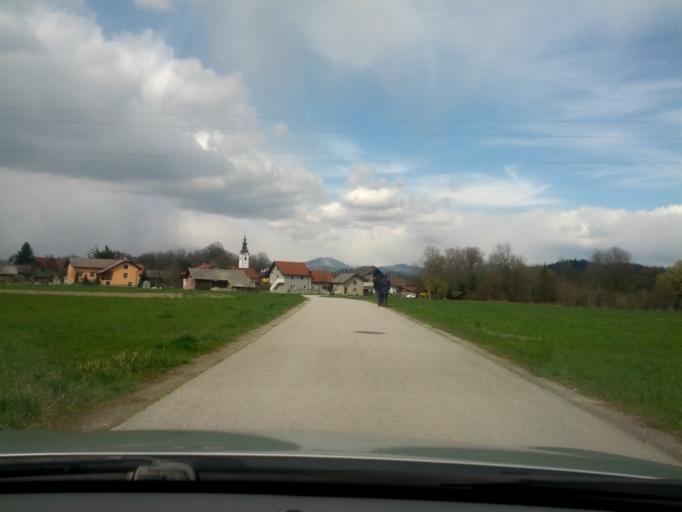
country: SI
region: Dol pri Ljubljani
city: Dol pri Ljubljani
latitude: 46.1107
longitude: 14.5980
